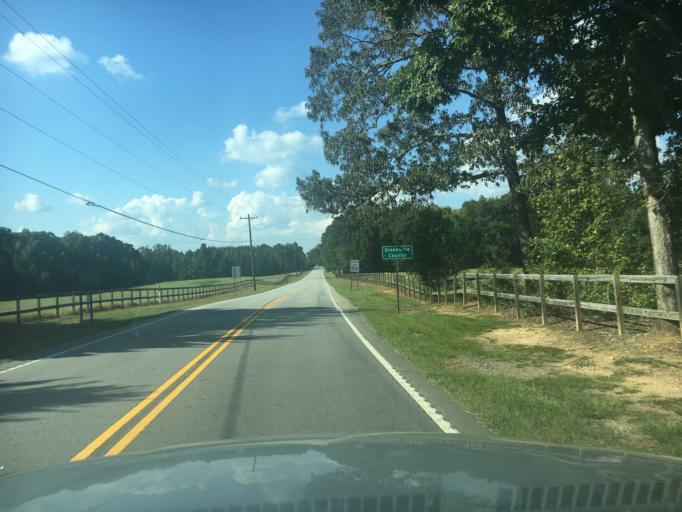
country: US
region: South Carolina
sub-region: Greenville County
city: Fountain Inn
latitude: 34.6004
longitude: -82.2294
